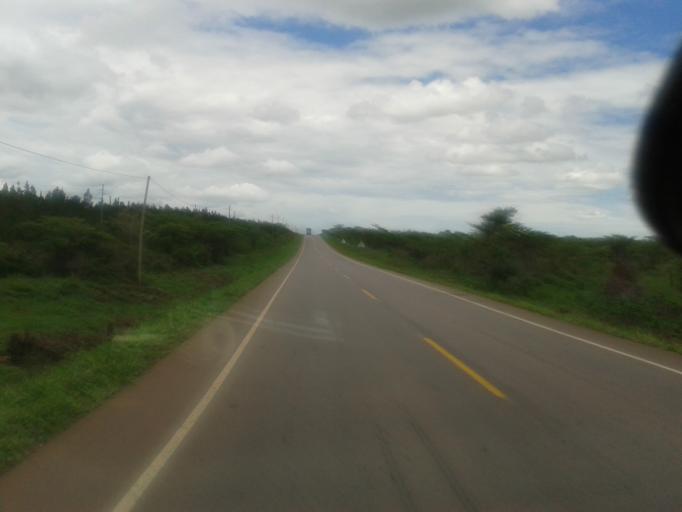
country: UG
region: Western Region
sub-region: Kiryandongo District
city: Masindi Port
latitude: 1.7582
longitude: 32.0210
